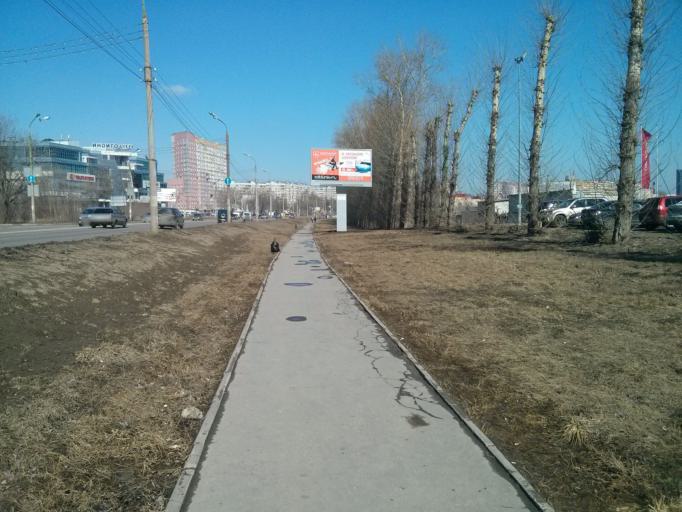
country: RU
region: Nizjnij Novgorod
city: Afonino
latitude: 56.2878
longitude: 44.0765
